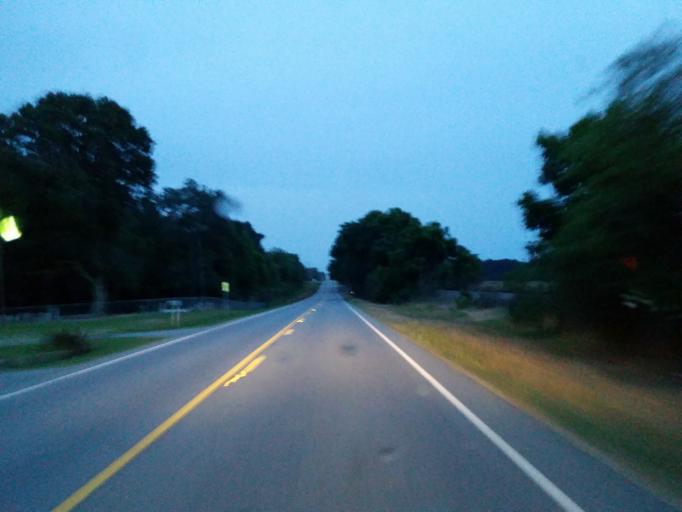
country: US
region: Georgia
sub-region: Turner County
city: Ashburn
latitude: 31.5871
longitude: -83.5758
